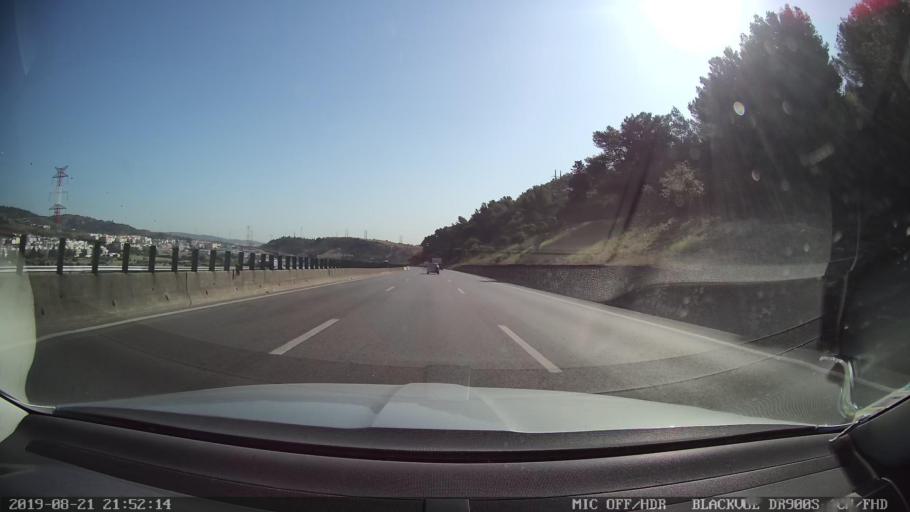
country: PT
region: Lisbon
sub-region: Vila Franca de Xira
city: Vialonga
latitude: 38.8668
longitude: -9.0749
